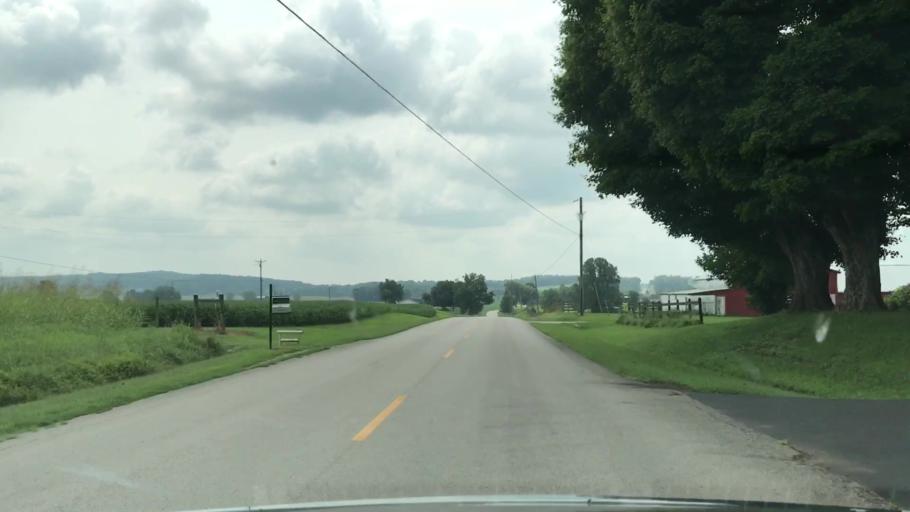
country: US
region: Kentucky
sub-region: Barren County
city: Cave City
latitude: 37.1035
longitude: -85.9786
